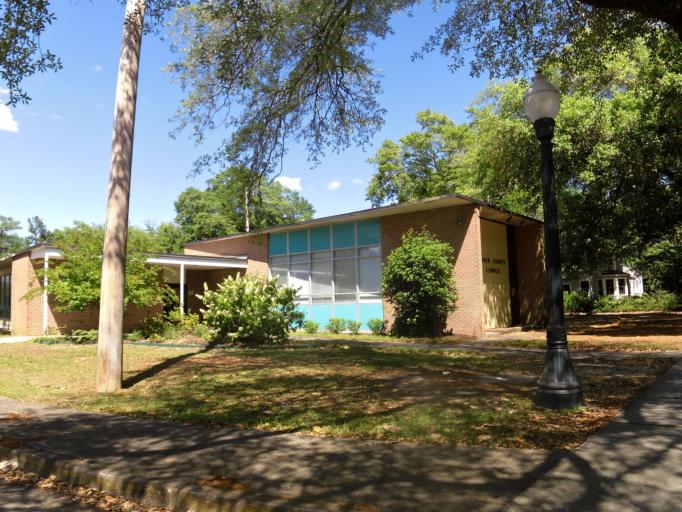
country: US
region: South Carolina
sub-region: Aiken County
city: Aiken
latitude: 33.5642
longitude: -81.7295
